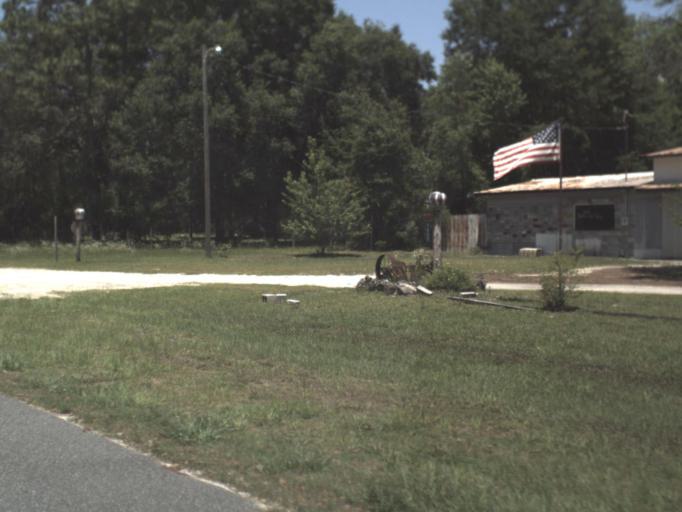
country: US
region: Florida
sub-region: Lafayette County
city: Mayo
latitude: 29.8852
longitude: -82.9553
